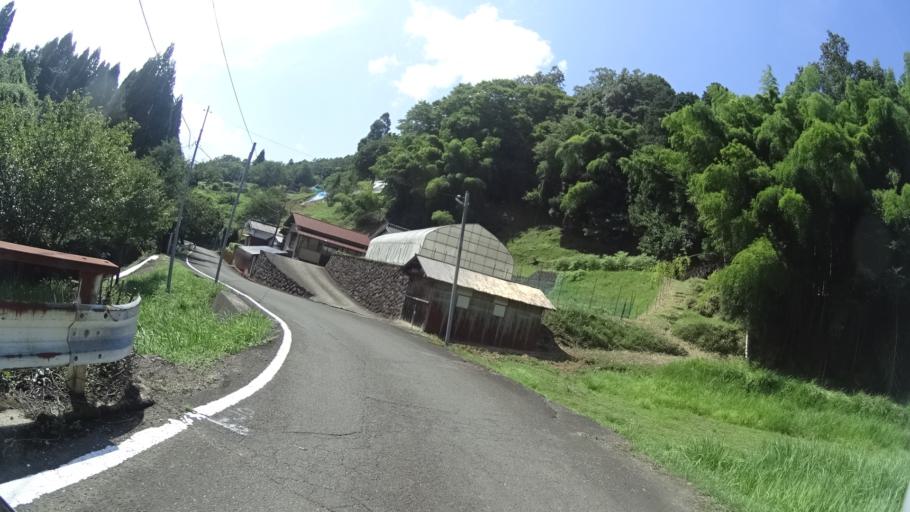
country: JP
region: Kyoto
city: Maizuru
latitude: 35.3850
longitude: 135.3583
